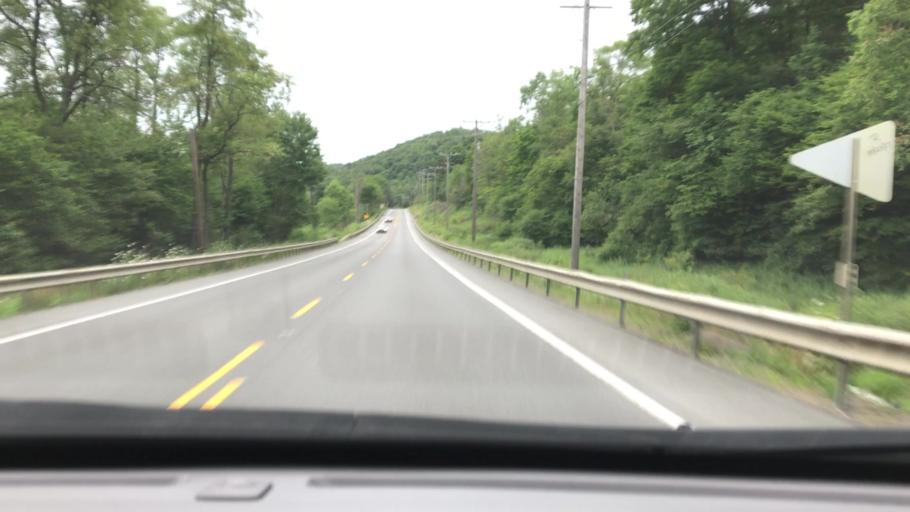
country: US
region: Pennsylvania
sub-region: Elk County
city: Johnsonburg
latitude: 41.5898
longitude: -78.6845
